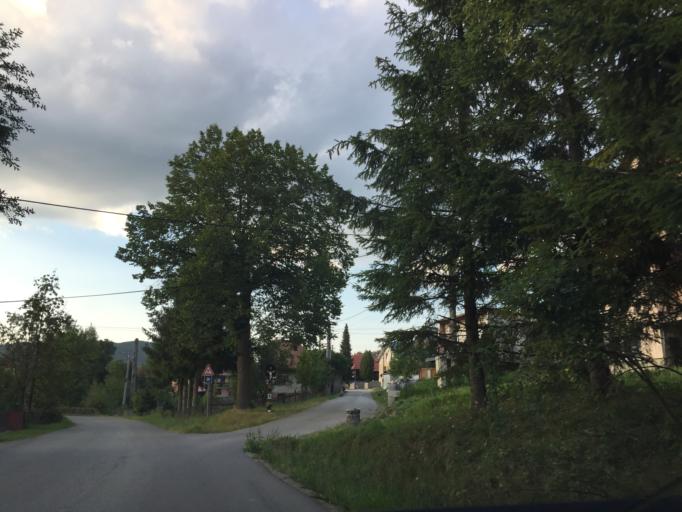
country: PL
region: Silesian Voivodeship
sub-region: Powiat zywiecki
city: Korbielow
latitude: 49.4786
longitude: 19.3828
